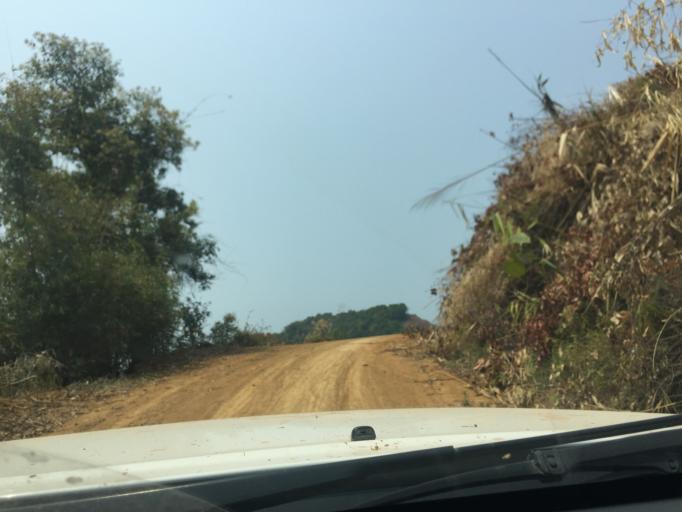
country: LA
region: Loungnamtha
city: Muang Nale
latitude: 20.6300
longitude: 101.6438
